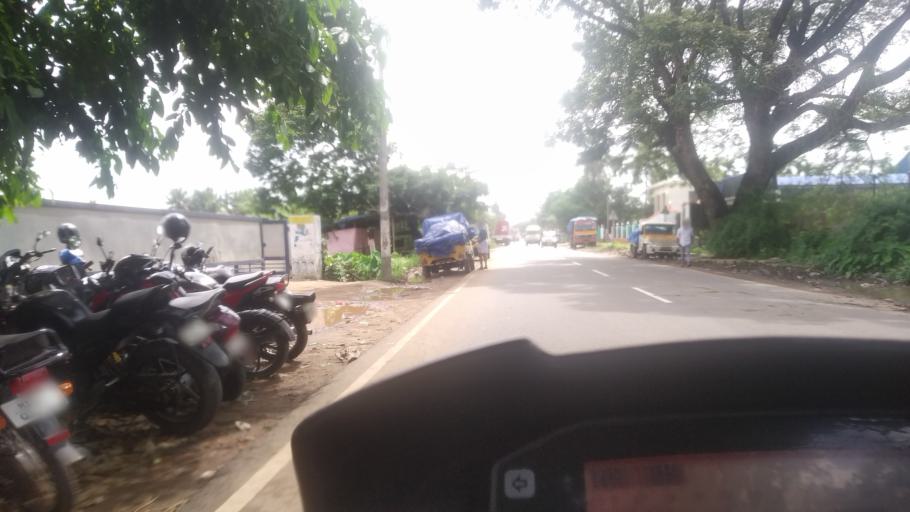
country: IN
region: Kerala
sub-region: Ernakulam
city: Aluva
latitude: 10.1279
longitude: 76.3069
